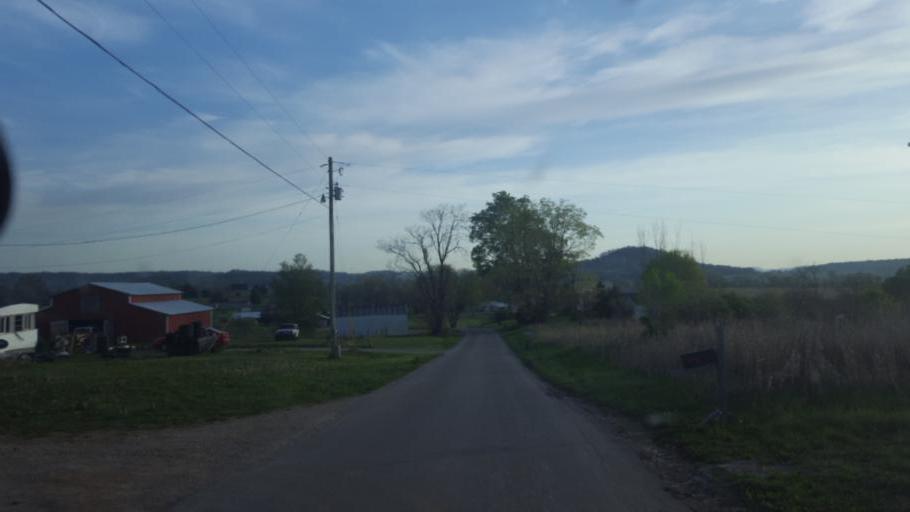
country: US
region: Kentucky
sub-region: Hart County
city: Horse Cave
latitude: 37.2307
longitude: -85.9322
